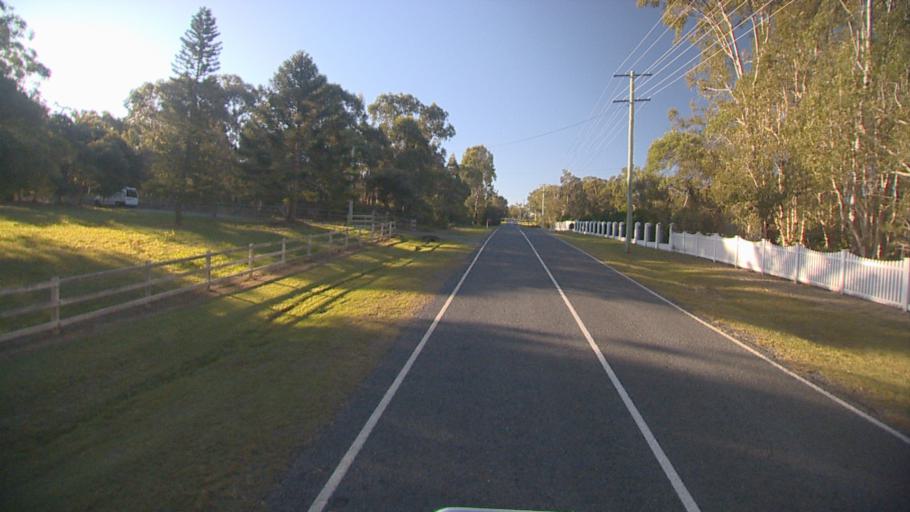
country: AU
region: Queensland
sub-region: Redland
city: Redland Bay
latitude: -27.6641
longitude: 153.2767
